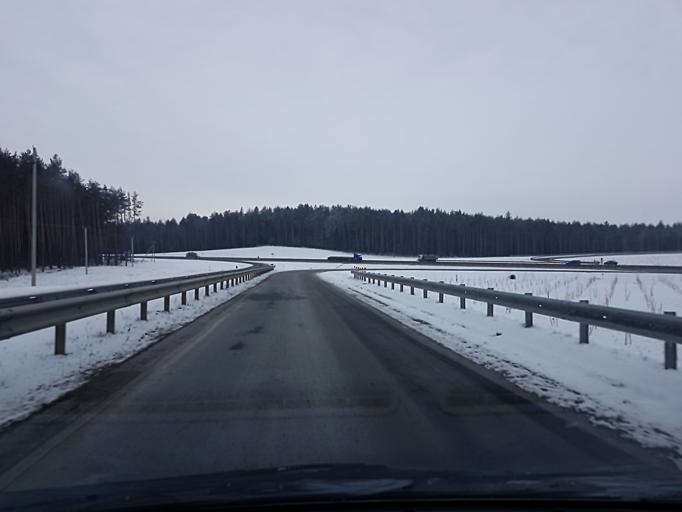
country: BY
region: Minsk
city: Rakaw
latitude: 53.9660
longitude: 27.0911
